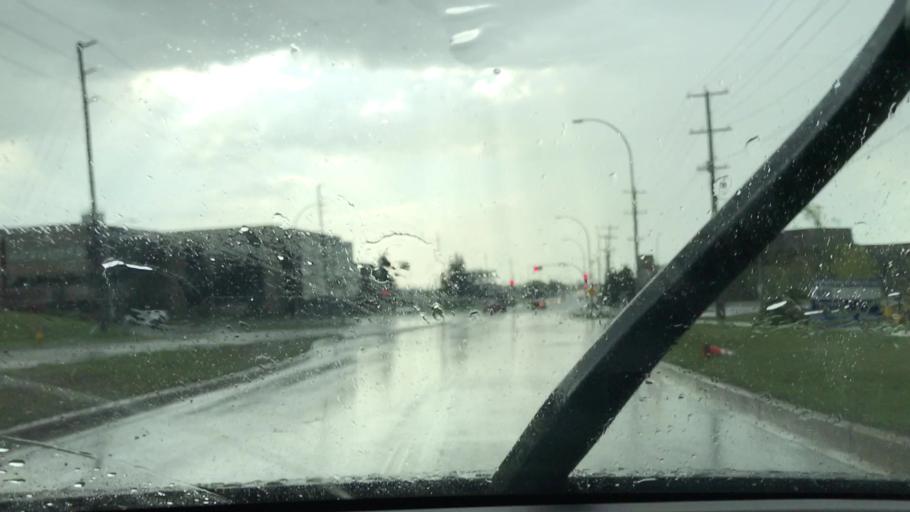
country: CA
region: Alberta
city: Edmonton
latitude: 53.4882
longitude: -113.4531
